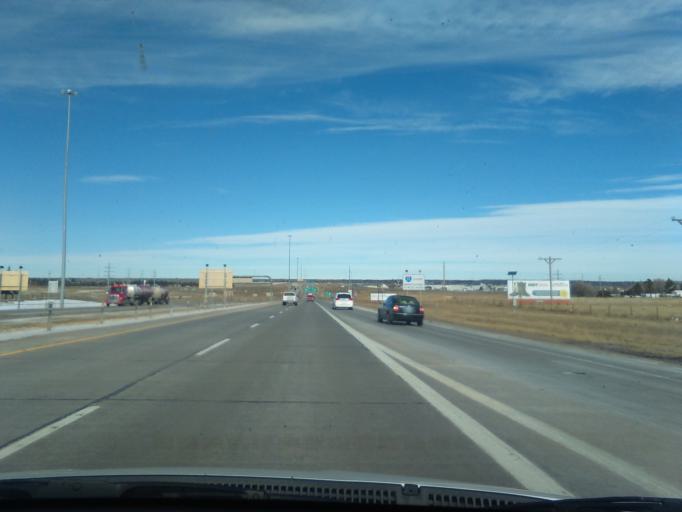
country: US
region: Wyoming
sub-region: Laramie County
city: South Greeley
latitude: 41.1031
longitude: -104.8504
